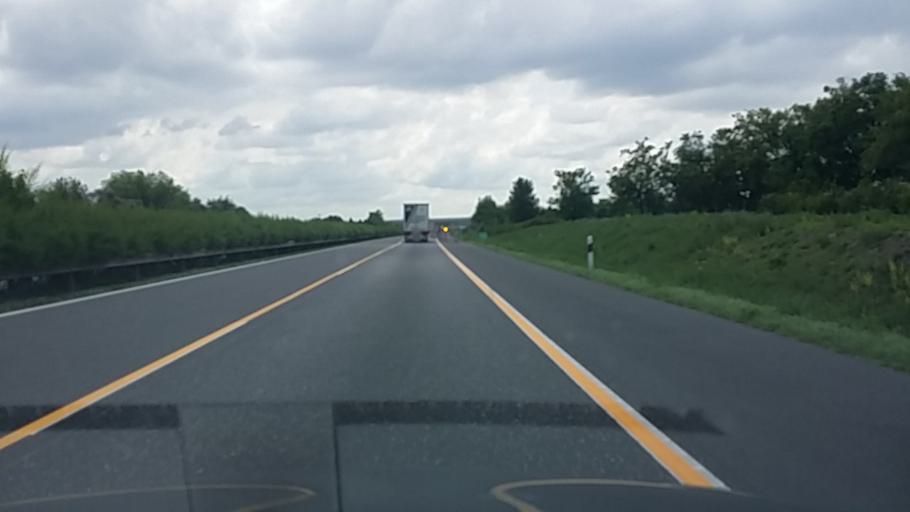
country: HU
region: Bacs-Kiskun
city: Kecskemet
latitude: 46.9439
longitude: 19.6200
